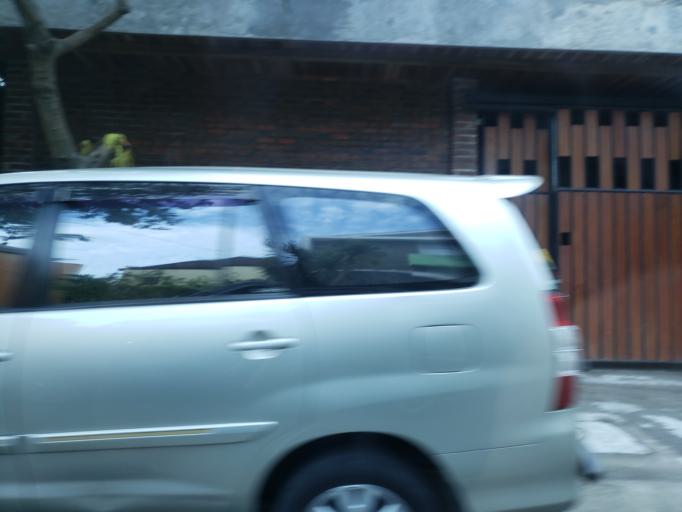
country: ID
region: Bali
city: Kuta
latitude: -8.6832
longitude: 115.1716
